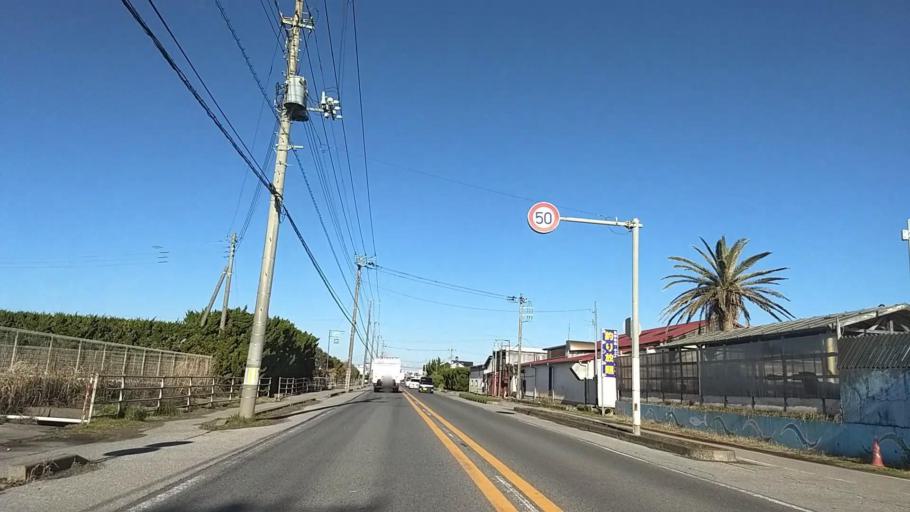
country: JP
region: Chiba
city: Togane
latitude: 35.5145
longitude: 140.4388
